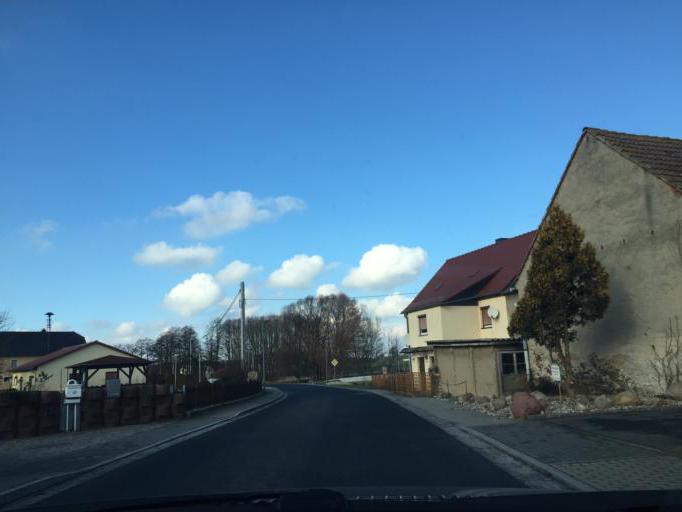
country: DE
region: Saxony
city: Thiendorf
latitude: 51.2779
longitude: 13.7480
